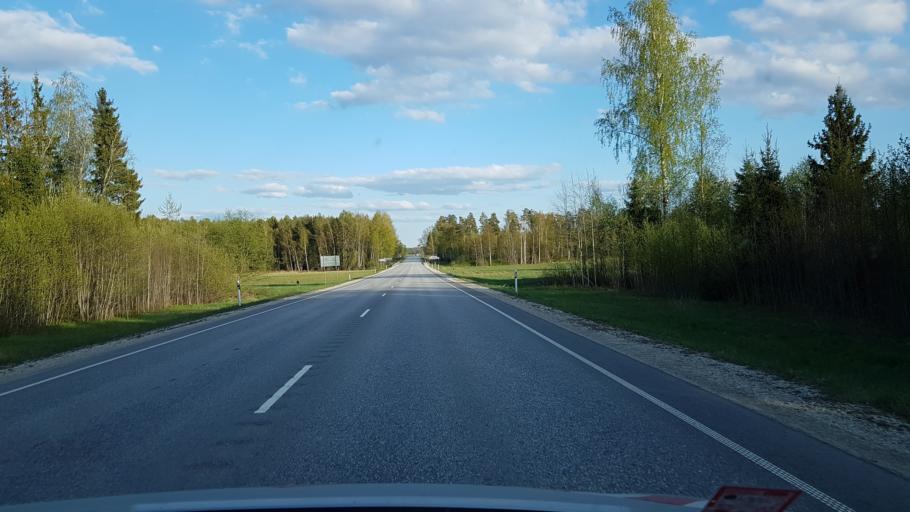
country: EE
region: Vorumaa
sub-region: Voru linn
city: Voru
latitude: 57.9195
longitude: 26.8101
